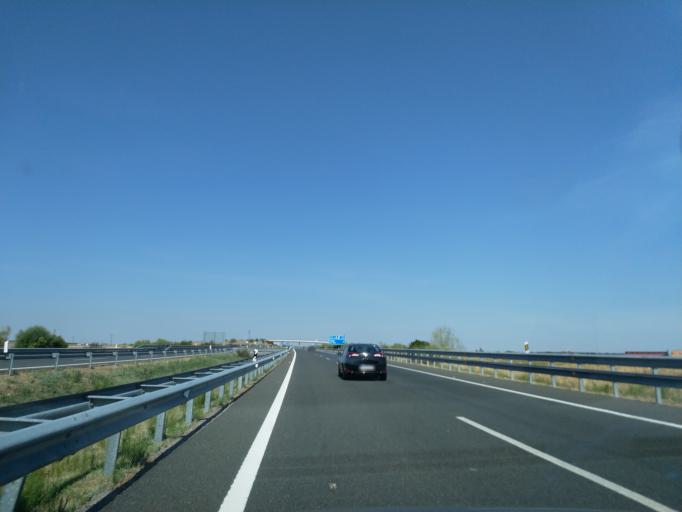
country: ES
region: Extremadura
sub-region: Provincia de Caceres
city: Aldea del Cano
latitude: 39.2804
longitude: -6.3258
